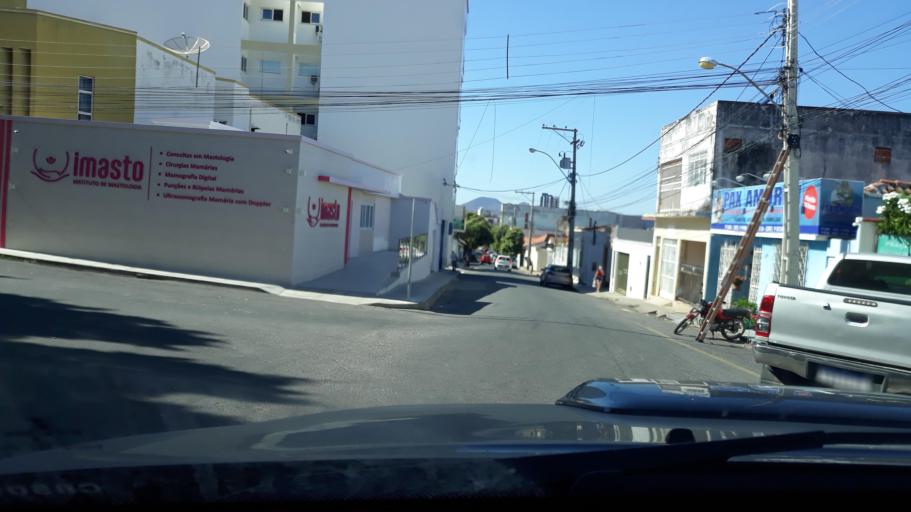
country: BR
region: Bahia
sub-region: Guanambi
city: Guanambi
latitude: -14.2237
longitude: -42.7827
